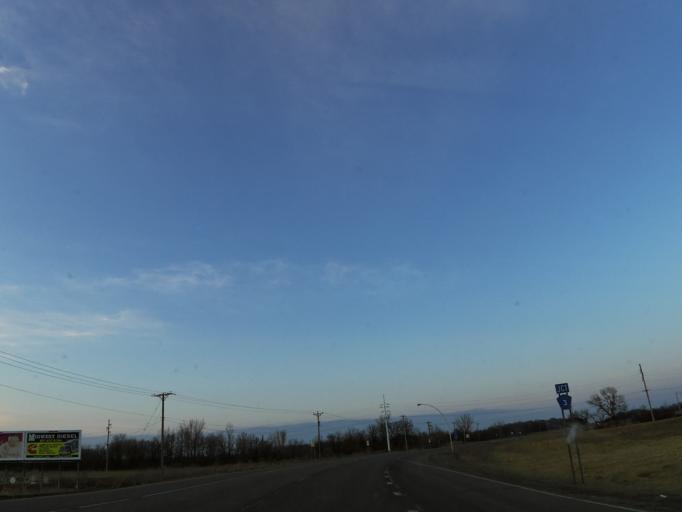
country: US
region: Minnesota
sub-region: Mower County
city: Austin
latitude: 43.6505
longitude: -92.9499
